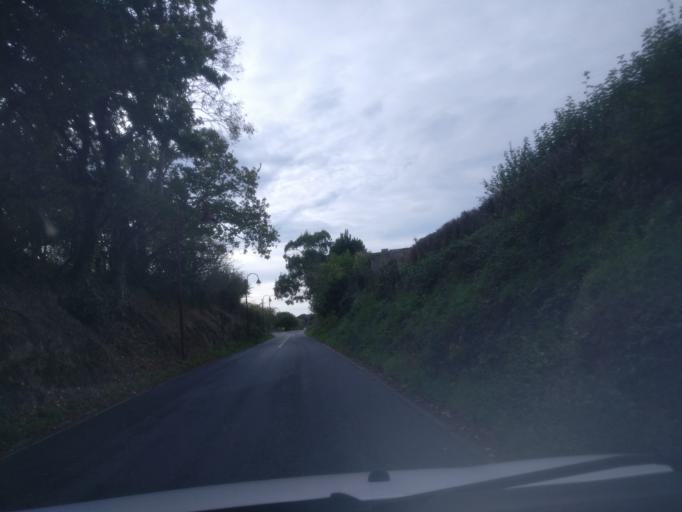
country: FR
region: Lower Normandy
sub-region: Departement de la Manche
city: Jullouville
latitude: 48.7479
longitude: -1.5547
